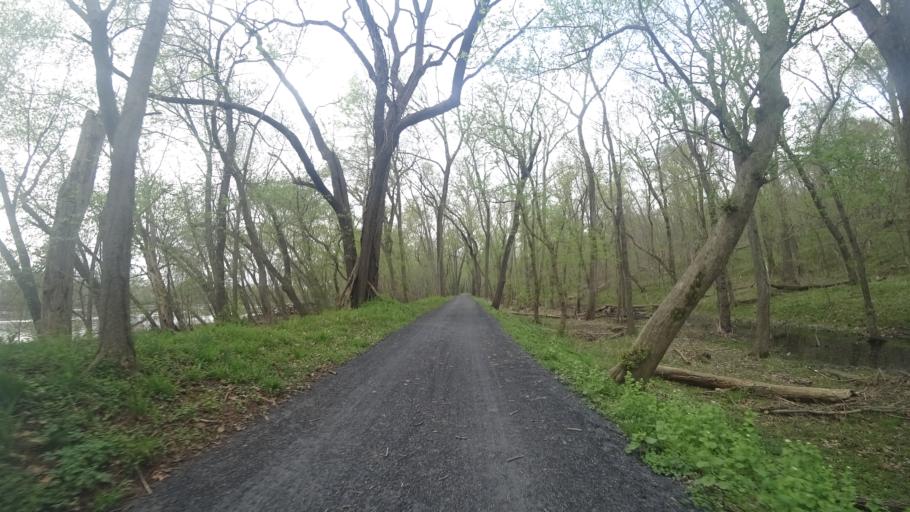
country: US
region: Virginia
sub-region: Loudoun County
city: University Center
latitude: 39.0944
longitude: -77.4676
